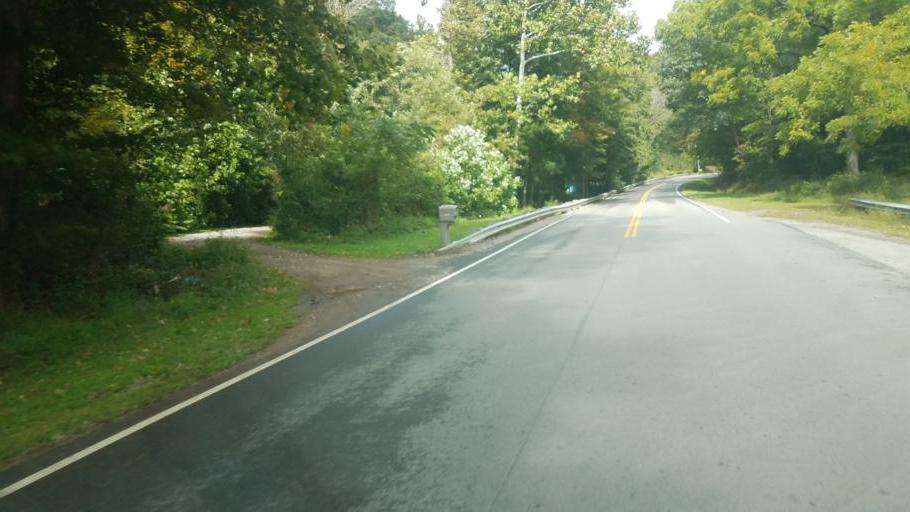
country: US
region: Ohio
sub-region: Scioto County
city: Sciotodale
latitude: 38.8731
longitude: -82.8157
